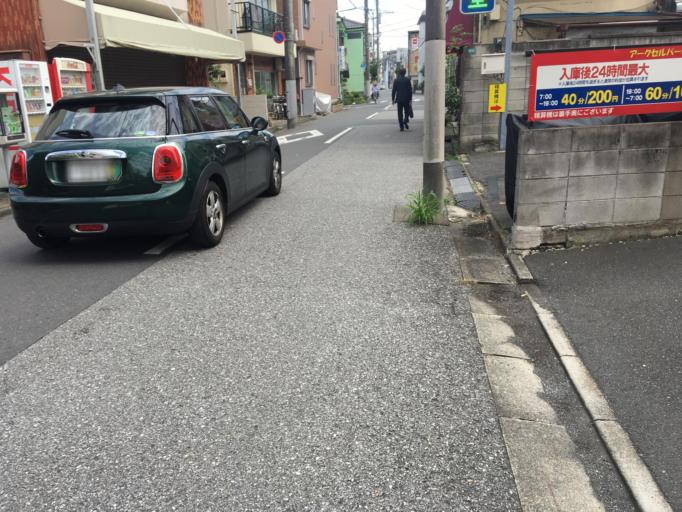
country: JP
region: Chiba
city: Matsudo
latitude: 35.7345
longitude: 139.8487
